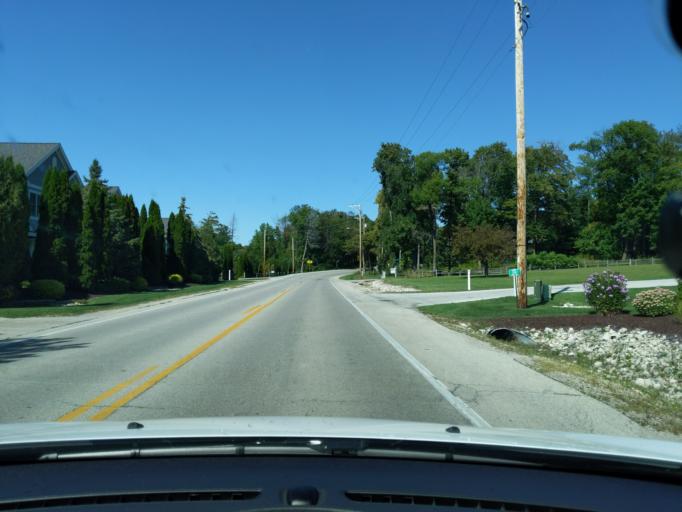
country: US
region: Wisconsin
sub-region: Door County
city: Sturgeon Bay
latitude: 45.2052
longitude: -87.1189
